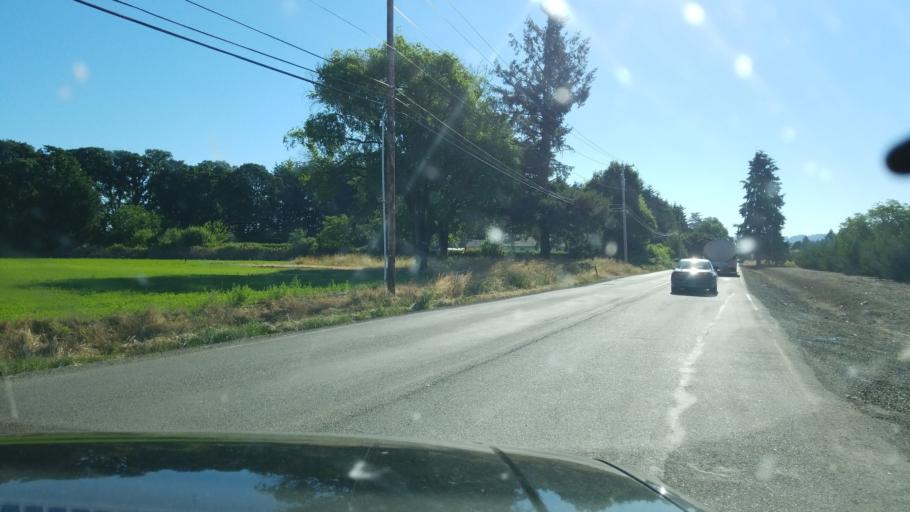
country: US
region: Oregon
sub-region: Yamhill County
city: Carlton
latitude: 45.2943
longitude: -123.2043
